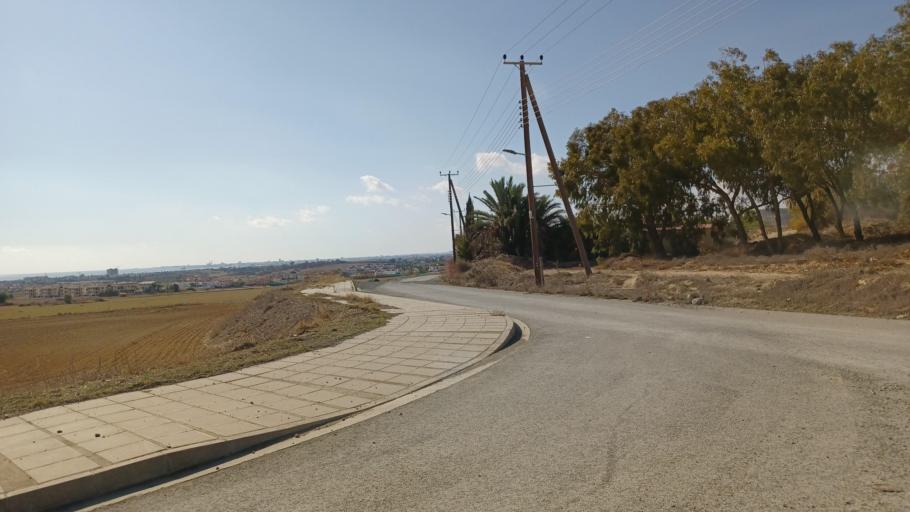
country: CY
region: Larnaka
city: Pyla
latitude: 35.0019
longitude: 33.6792
